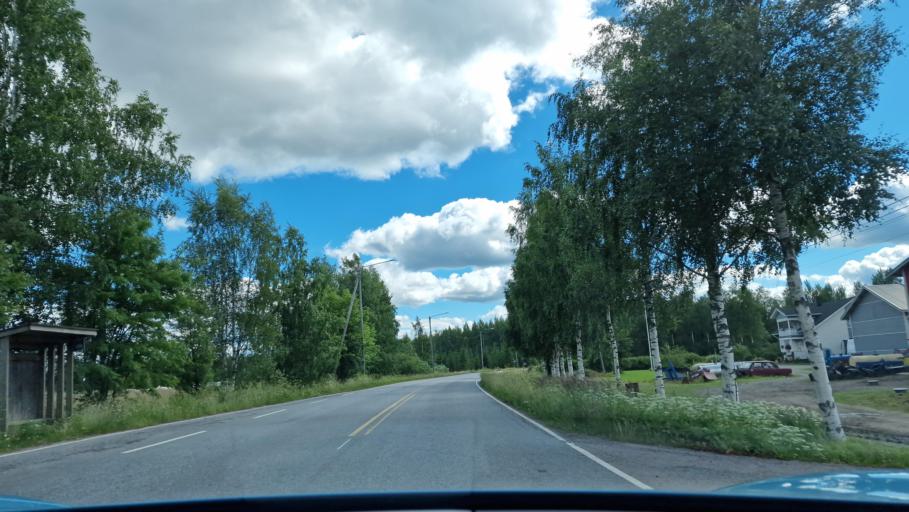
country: FI
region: Southern Ostrobothnia
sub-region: Jaerviseutu
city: Soini
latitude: 62.8426
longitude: 24.3276
